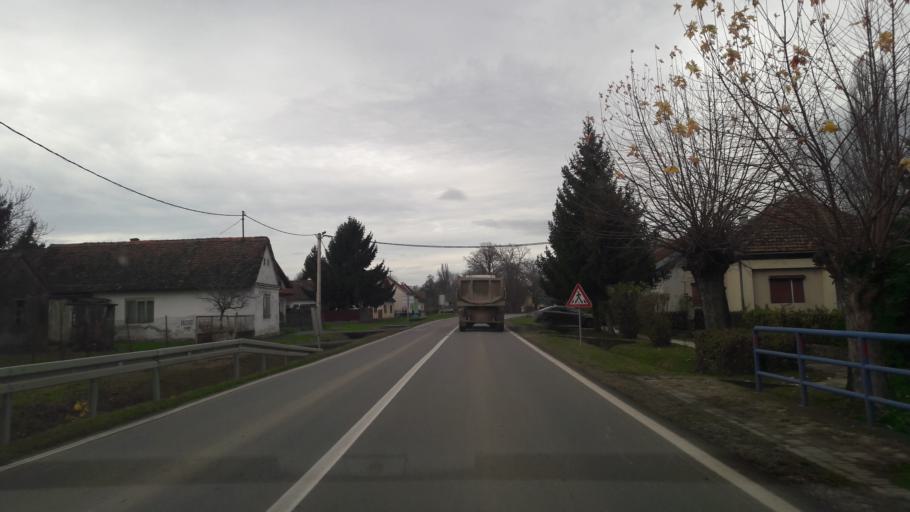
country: HR
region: Osjecko-Baranjska
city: Fericanci
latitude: 45.5242
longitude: 17.9683
